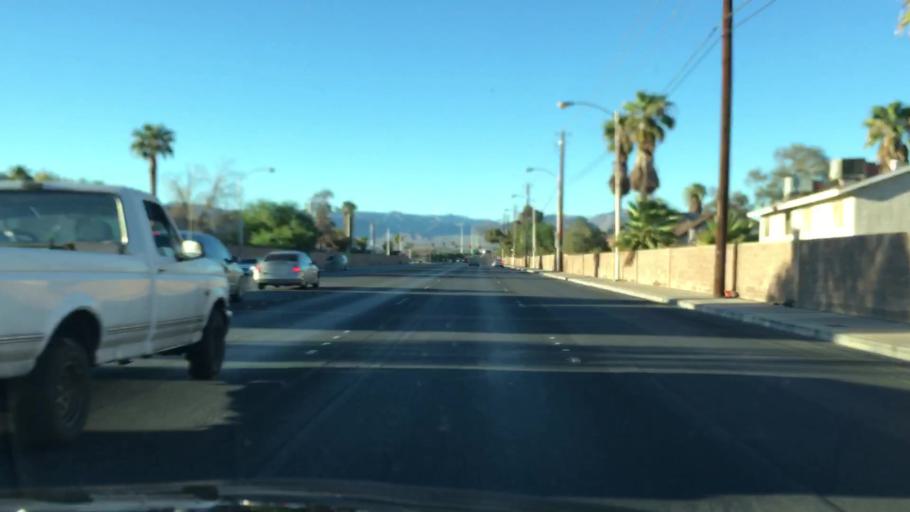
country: US
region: Nevada
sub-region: Clark County
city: Sunrise Manor
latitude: 36.2299
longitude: -115.0801
